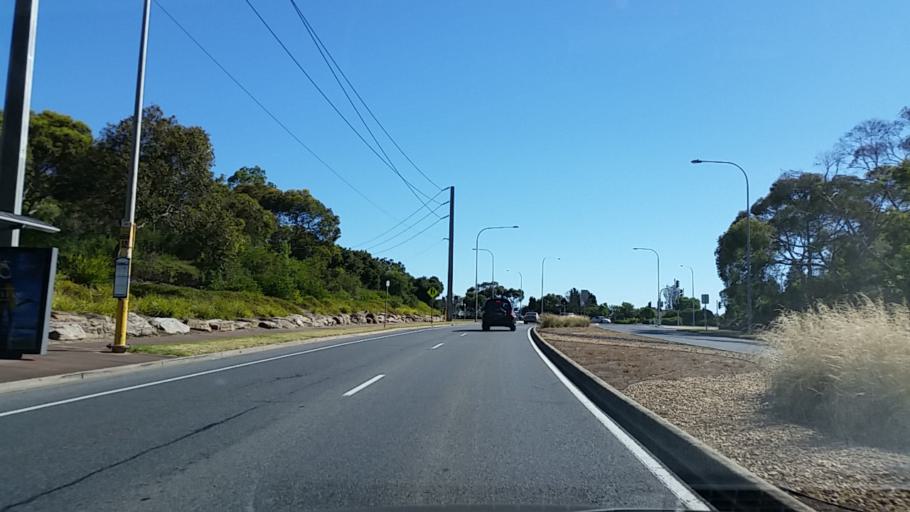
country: AU
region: South Australia
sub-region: Tea Tree Gully
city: Modbury
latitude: -34.8105
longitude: 138.6760
